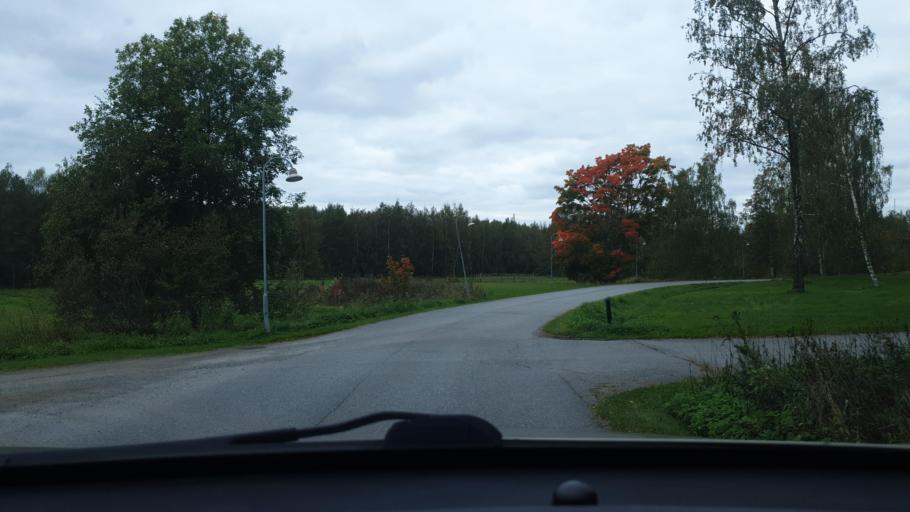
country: FI
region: Ostrobothnia
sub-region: Vaasa
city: Teeriniemi
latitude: 63.0866
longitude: 21.6764
